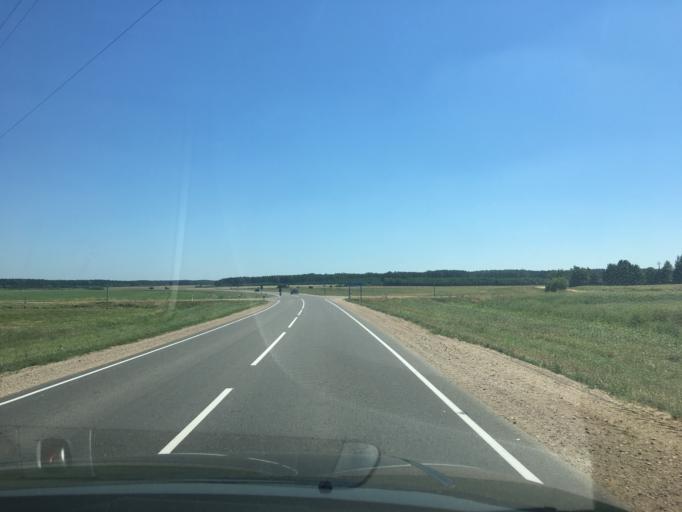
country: BY
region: Grodnenskaya
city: Iwye
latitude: 53.9132
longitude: 25.7721
